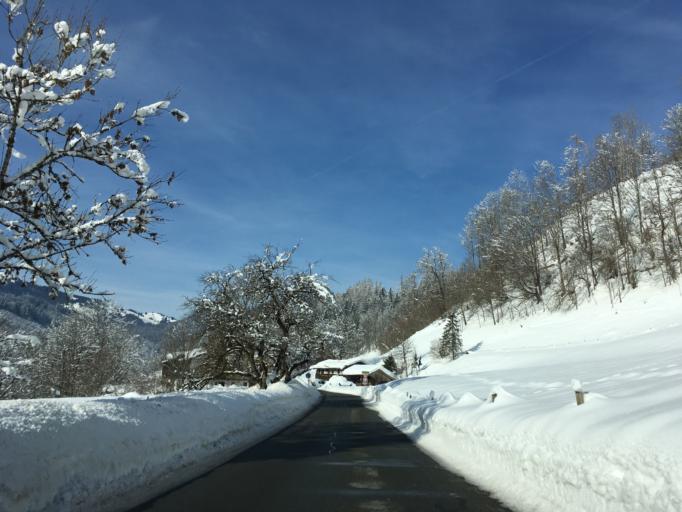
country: DE
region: Bavaria
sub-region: Upper Bavaria
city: Burg Unter-Falkenstein
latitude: 47.6668
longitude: 12.1068
